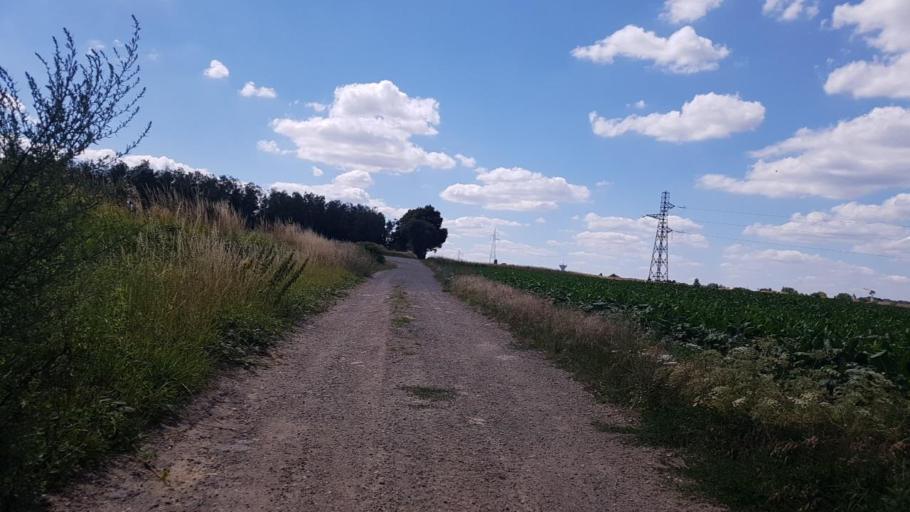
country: FR
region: Ile-de-France
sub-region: Departement de Seine-et-Marne
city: Moussy-le-Vieux
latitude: 49.0562
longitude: 2.6160
